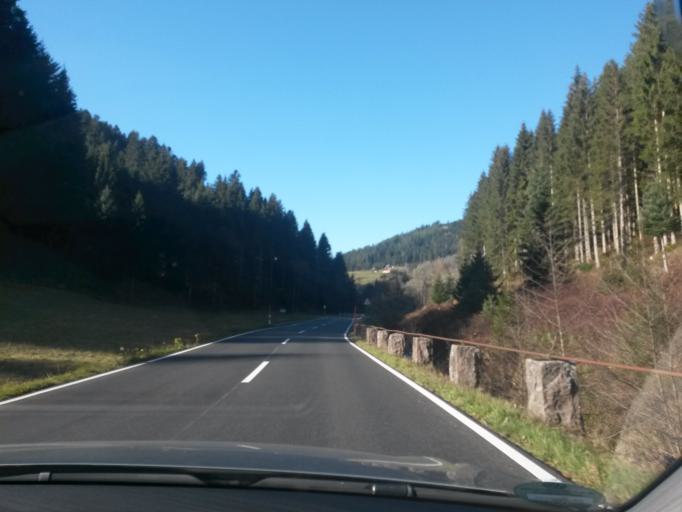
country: DE
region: Baden-Wuerttemberg
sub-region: Karlsruhe Region
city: Bad Rippoldsau-Schapbach
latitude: 48.4431
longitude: 8.3131
